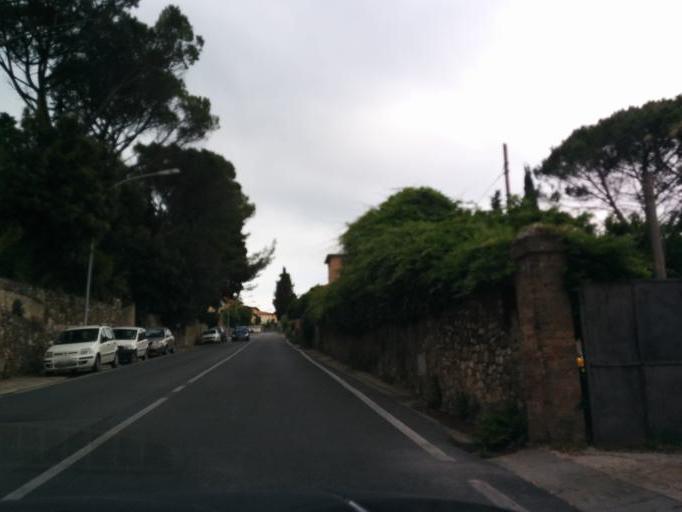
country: IT
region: Tuscany
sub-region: Province of Florence
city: San Casciano in Val di Pesa
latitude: 43.6495
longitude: 11.1801
